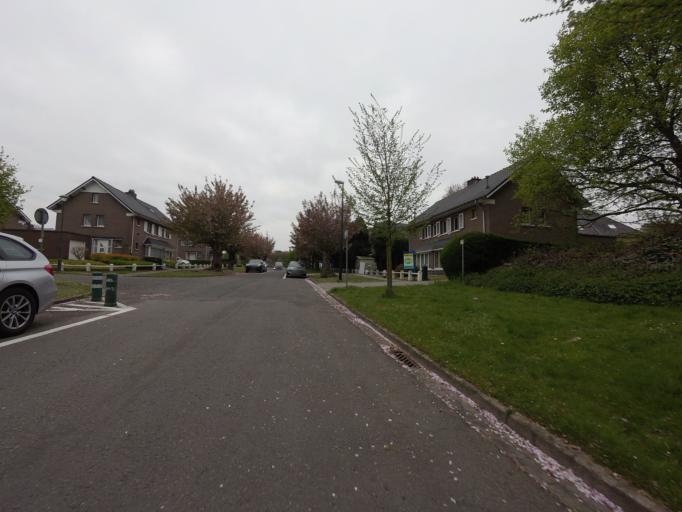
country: BE
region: Flanders
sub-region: Provincie Vlaams-Brabant
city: Vilvoorde
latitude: 50.9210
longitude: 4.4043
